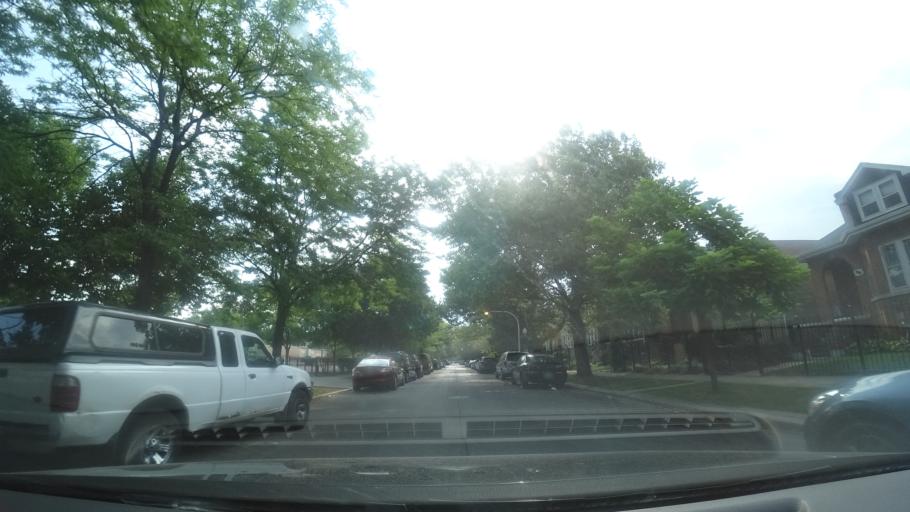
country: US
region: Illinois
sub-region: Cook County
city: Elmwood Park
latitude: 41.9295
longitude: -87.7604
